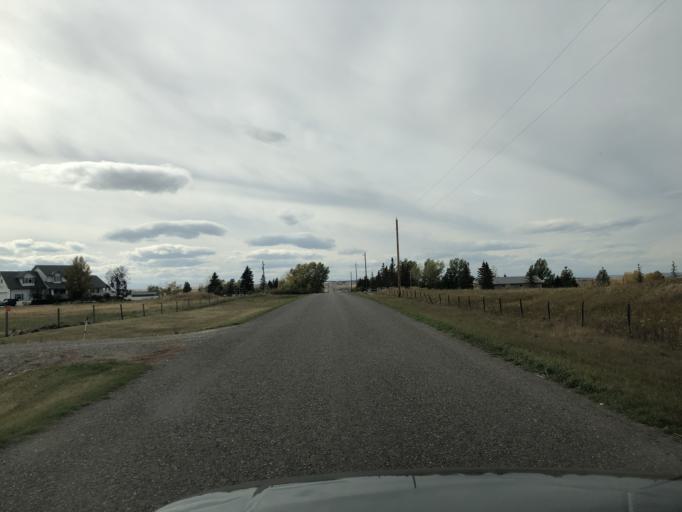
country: CA
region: Alberta
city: Okotoks
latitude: 50.6886
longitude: -113.9658
